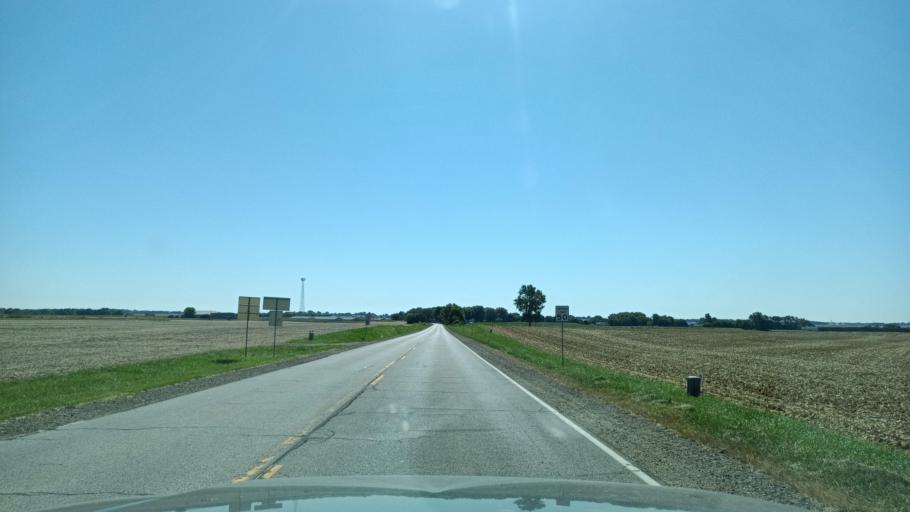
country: US
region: Illinois
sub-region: Peoria County
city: Elmwood
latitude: 40.8376
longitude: -89.8783
